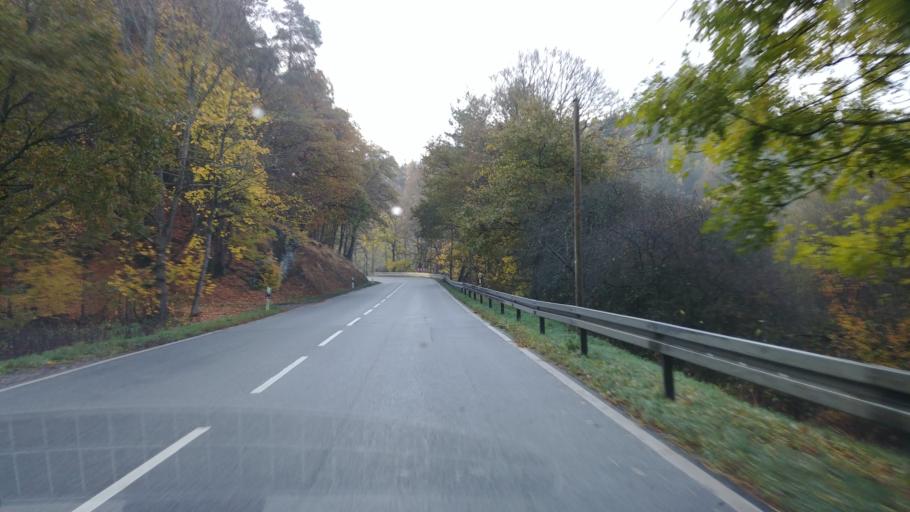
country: DE
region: Hesse
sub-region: Regierungsbezirk Darmstadt
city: Bad Schwalbach
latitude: 50.1346
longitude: 8.1017
